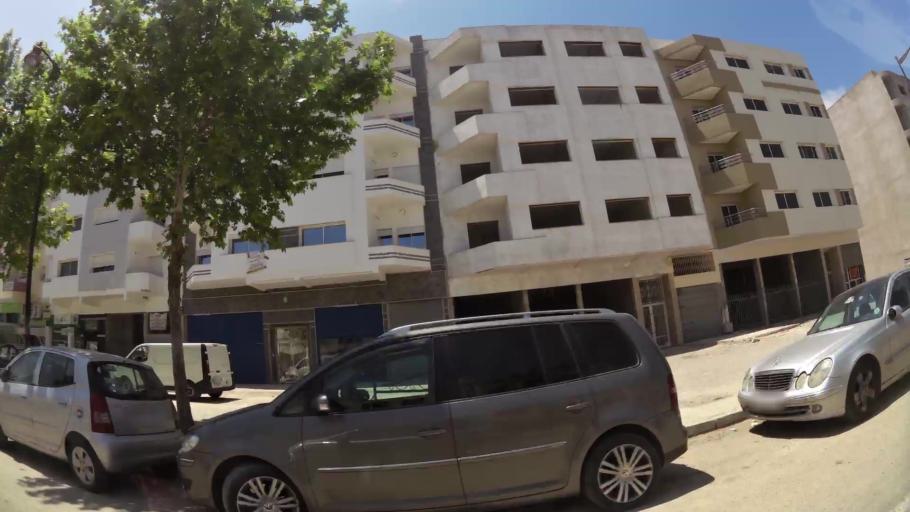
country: MA
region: Fes-Boulemane
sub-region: Fes
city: Fes
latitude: 34.0185
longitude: -5.0531
